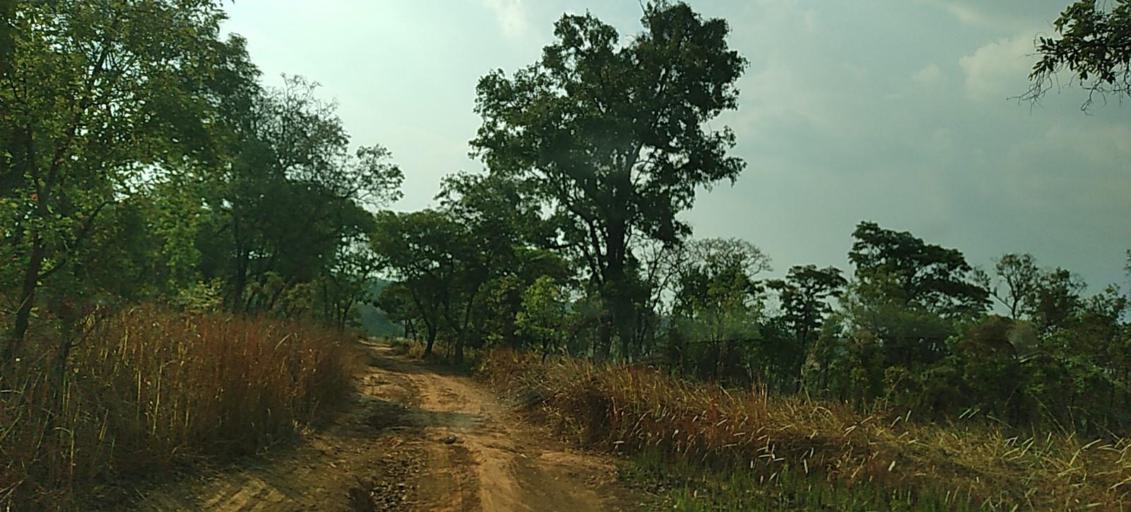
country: ZM
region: North-Western
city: Solwezi
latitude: -12.0678
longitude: 26.1800
